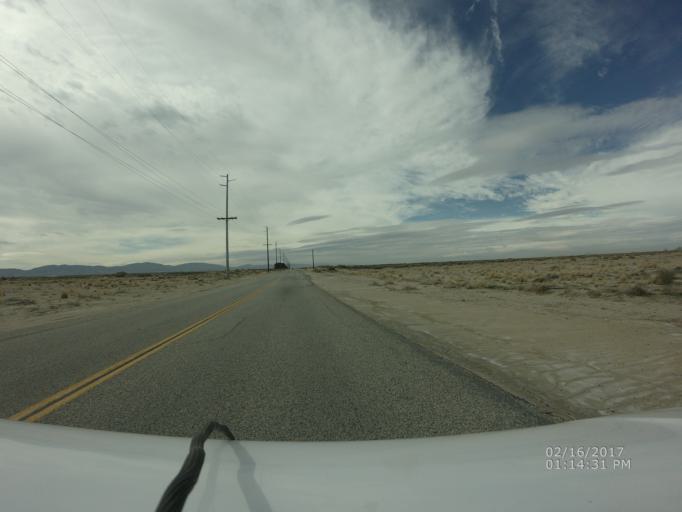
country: US
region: California
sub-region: Los Angeles County
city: Littlerock
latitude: 34.6313
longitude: -118.0128
